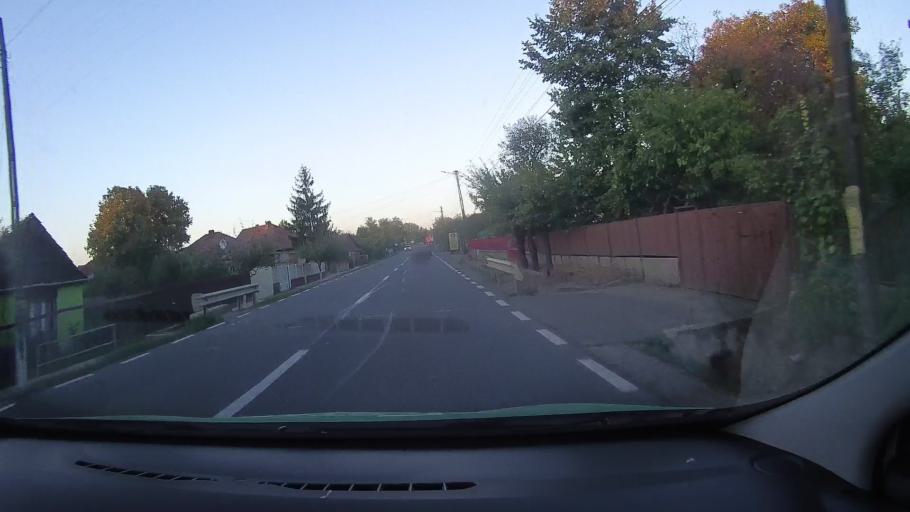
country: RO
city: Szekelyhid
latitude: 47.3341
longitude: 22.0870
